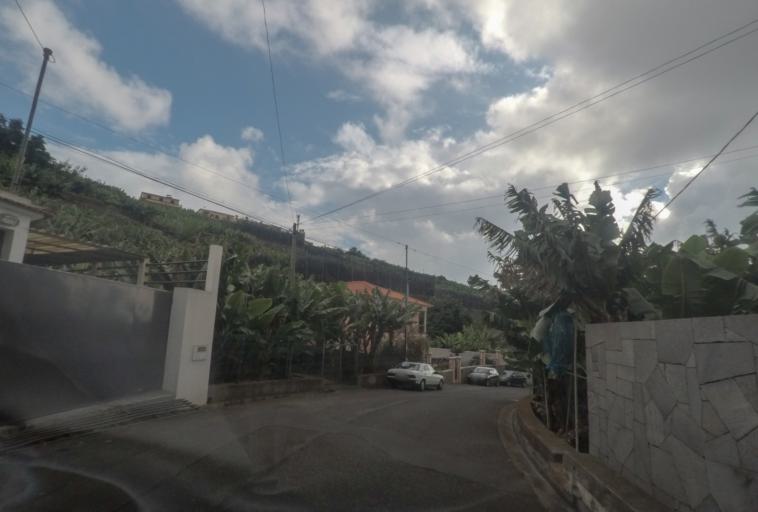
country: PT
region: Madeira
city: Camara de Lobos
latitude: 32.6582
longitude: -16.9570
